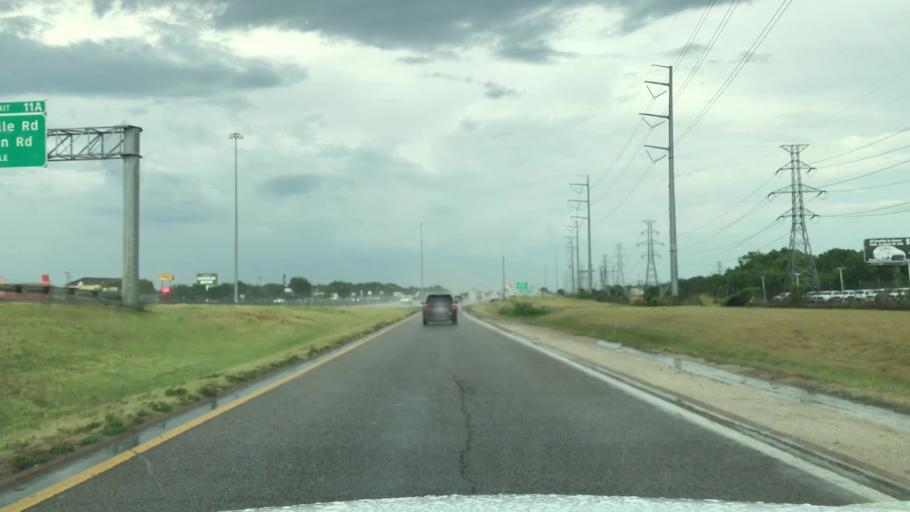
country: US
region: Texas
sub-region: Dallas County
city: Garland
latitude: 32.8626
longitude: -96.6599
